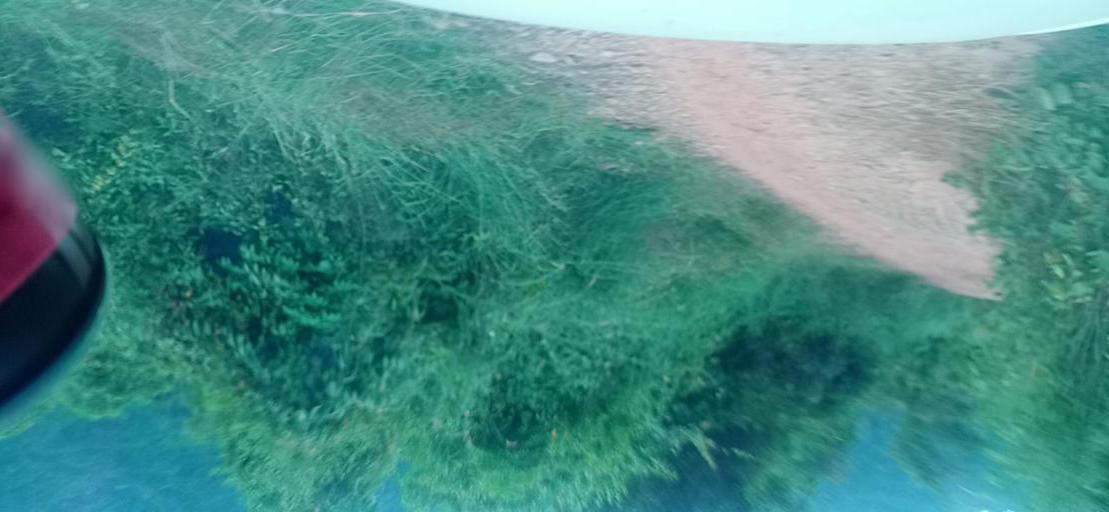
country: TH
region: Changwat Bueng Kan
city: Pak Khat
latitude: 18.5610
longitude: 103.2918
